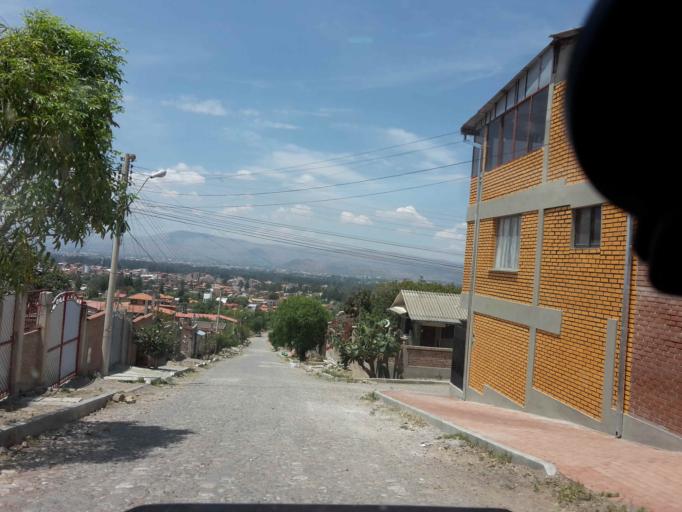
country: BO
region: Cochabamba
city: Cochabamba
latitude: -17.3220
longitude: -66.2226
